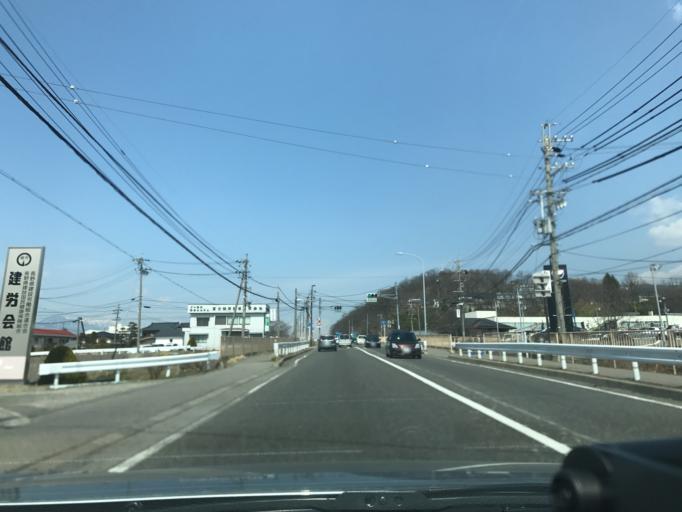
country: JP
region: Nagano
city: Matsumoto
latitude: 36.2395
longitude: 137.9554
